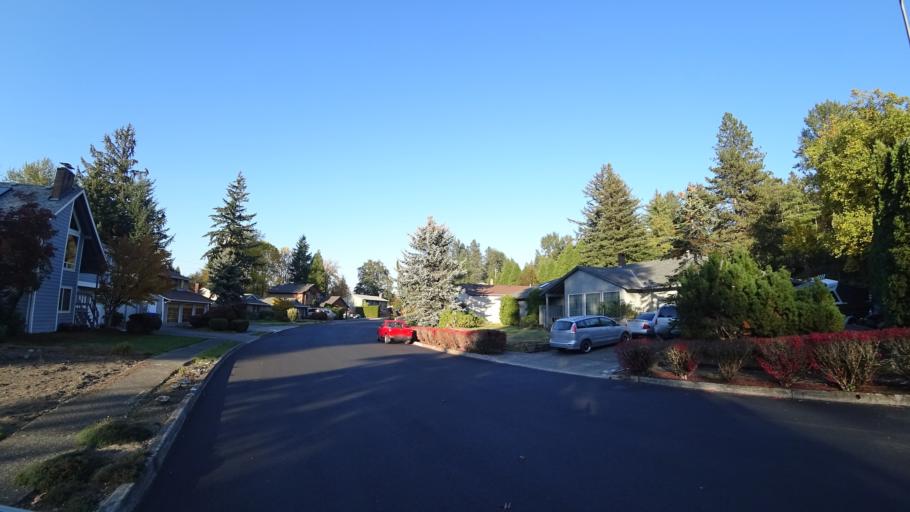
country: US
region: Oregon
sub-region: Multnomah County
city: Gresham
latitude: 45.4886
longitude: -122.4490
